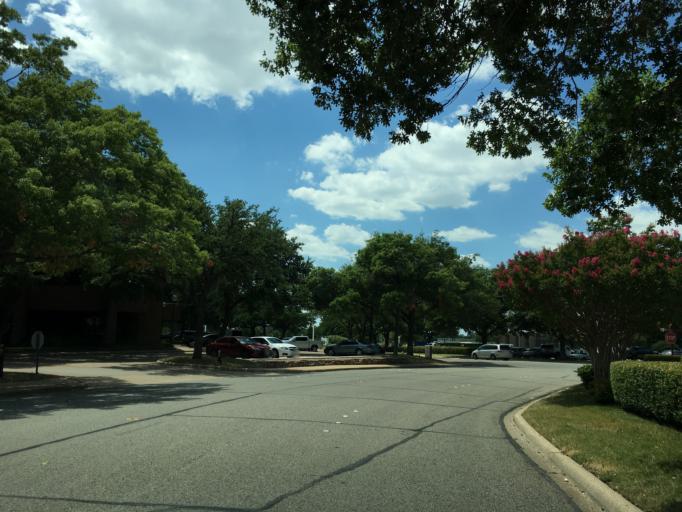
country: US
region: Texas
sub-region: Dallas County
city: Addison
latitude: 32.9281
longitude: -96.8431
